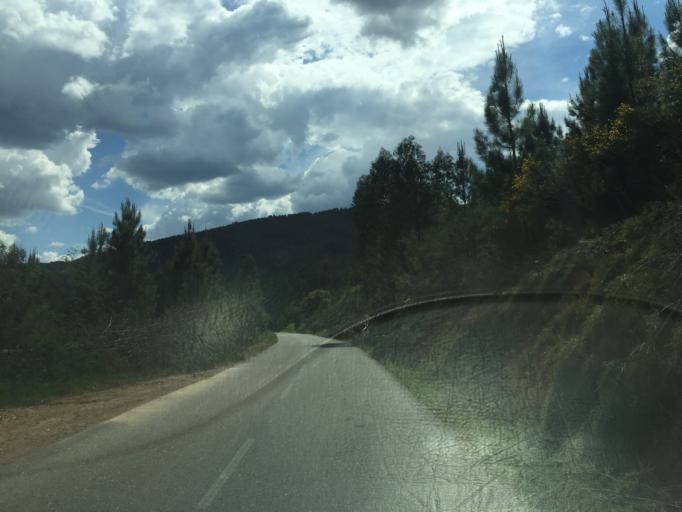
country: PT
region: Coimbra
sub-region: Pampilhosa da Serra
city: Pampilhosa da Serra
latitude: 40.0551
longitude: -7.8091
